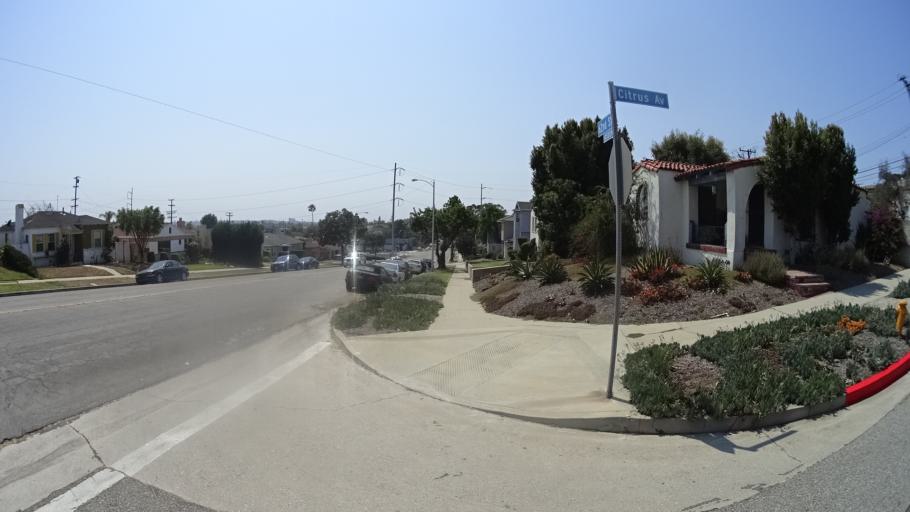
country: US
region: California
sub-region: Los Angeles County
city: View Park-Windsor Hills
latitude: 33.9835
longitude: -118.3563
